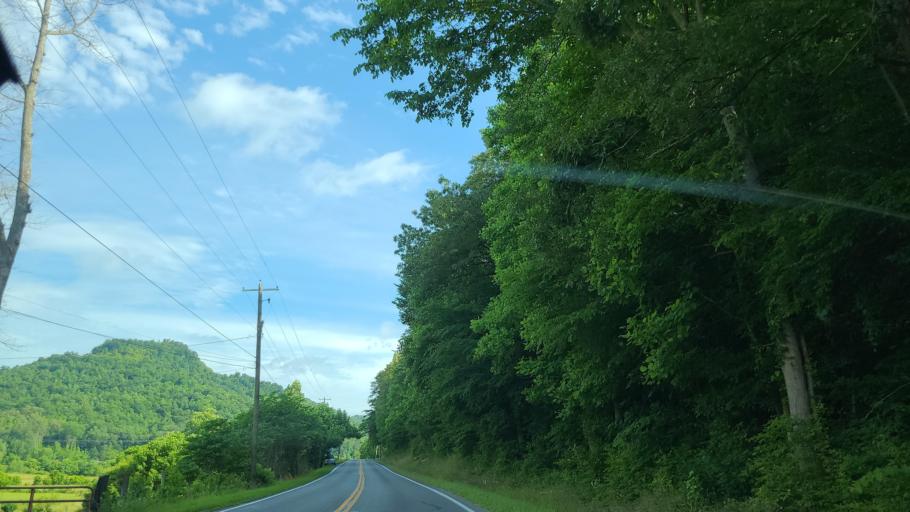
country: US
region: Kentucky
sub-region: Bell County
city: Pineville
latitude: 36.7730
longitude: -83.7706
